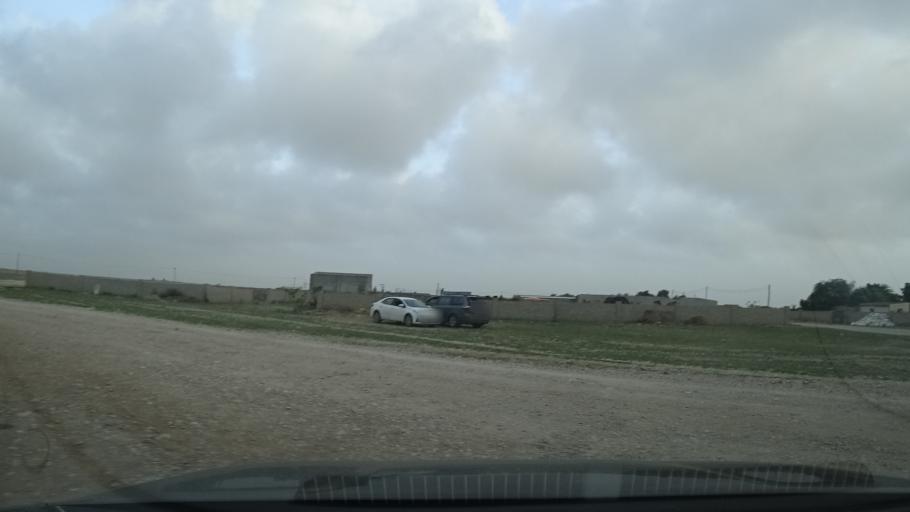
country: OM
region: Zufar
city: Salalah
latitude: 17.1016
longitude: 54.2353
